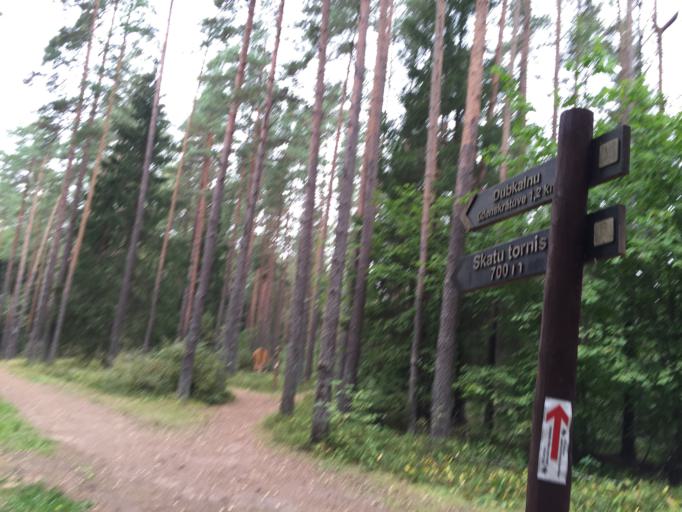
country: LV
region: Ogre
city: Ogre
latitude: 56.8336
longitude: 24.5749
